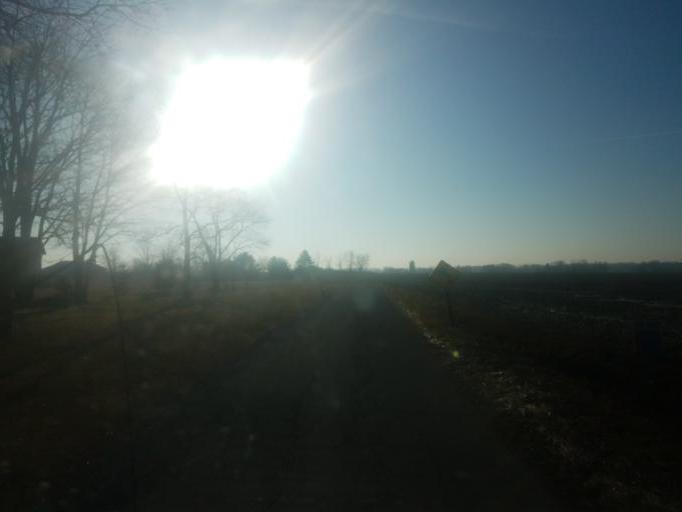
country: US
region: Ohio
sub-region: Crawford County
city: Bucyrus
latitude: 40.8349
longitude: -82.9473
